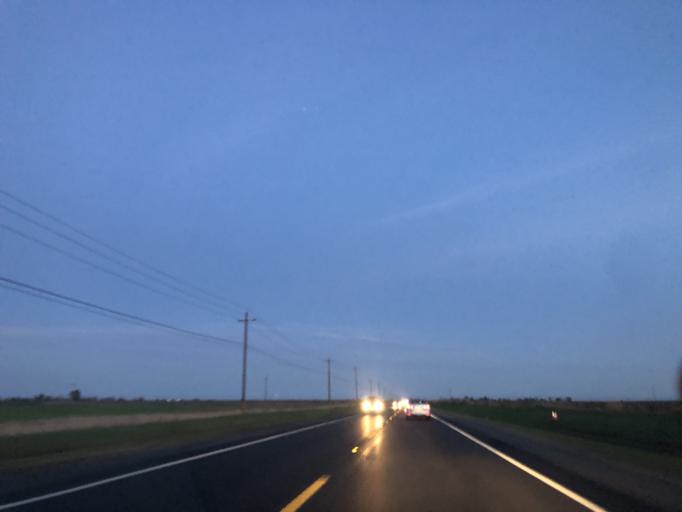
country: US
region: California
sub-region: Yolo County
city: Esparto
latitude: 38.6856
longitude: -121.9937
